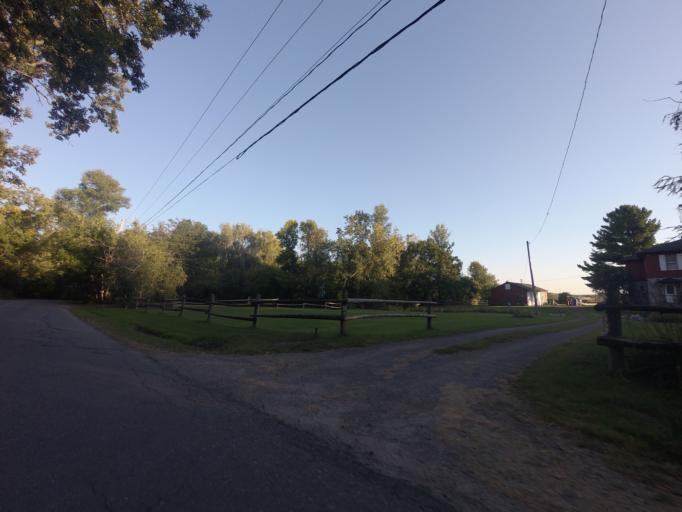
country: CA
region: Quebec
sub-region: Monteregie
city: Hudson
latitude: 45.4827
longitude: -74.2075
